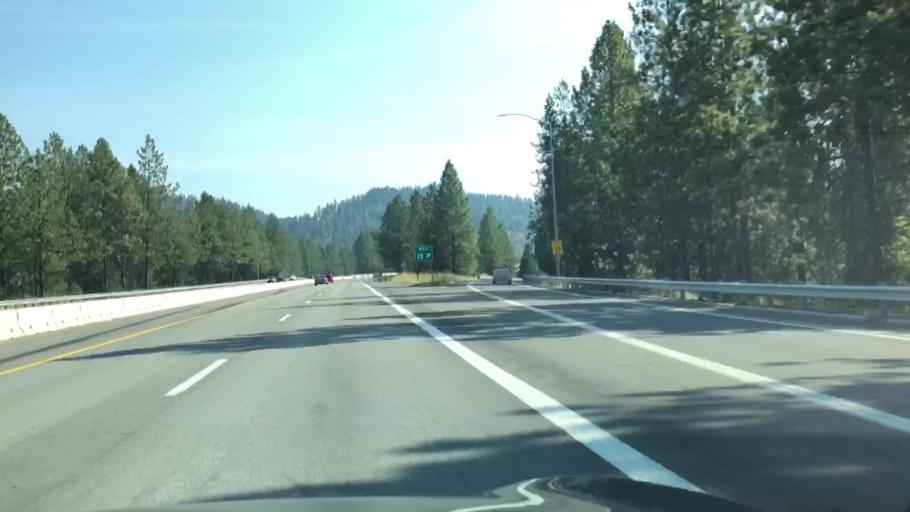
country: US
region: Idaho
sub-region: Kootenai County
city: Coeur d'Alene
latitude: 47.6781
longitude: -116.7546
